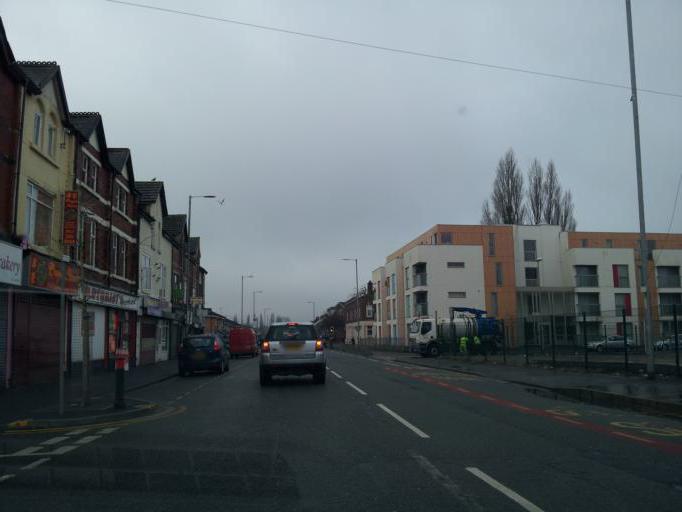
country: GB
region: England
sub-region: Manchester
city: Blackley
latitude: 53.5113
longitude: -2.2150
